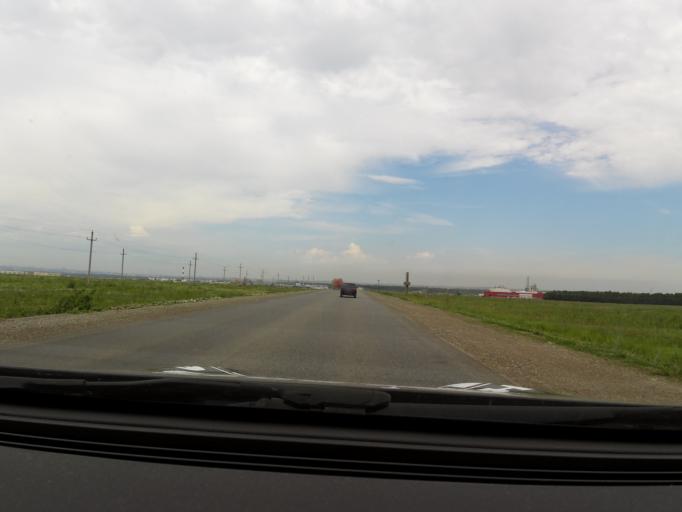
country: RU
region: Bashkortostan
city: Iglino
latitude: 54.7548
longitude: 56.2829
